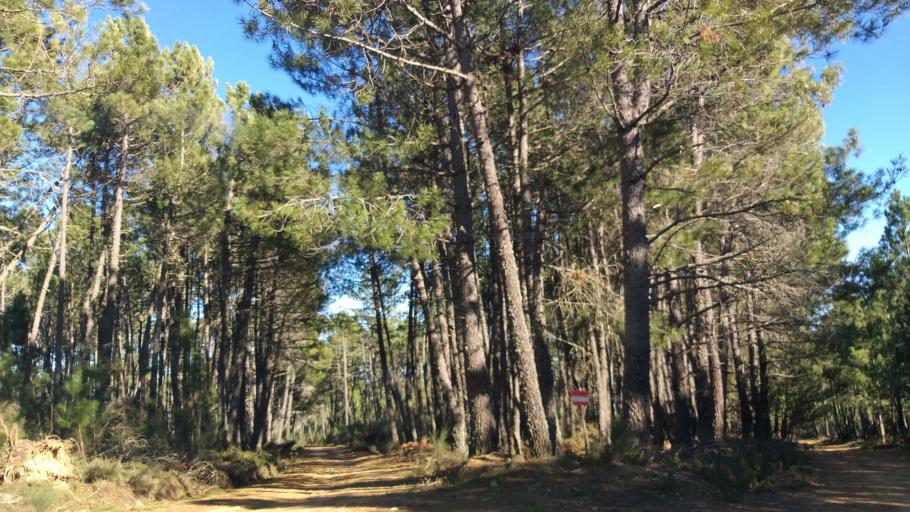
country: PT
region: Guarda
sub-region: Celorico da Beira
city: Celorico da Beira
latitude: 40.5144
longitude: -7.4069
